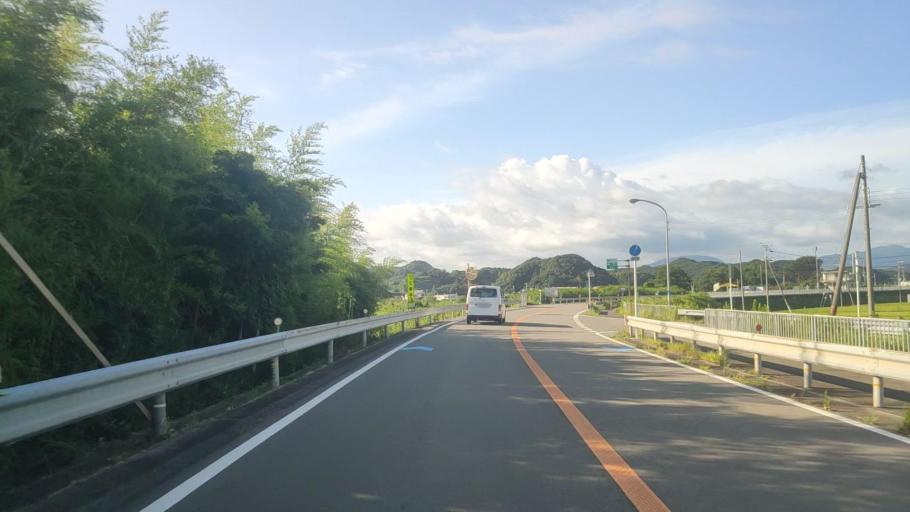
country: JP
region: Wakayama
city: Tanabe
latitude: 33.6761
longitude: 135.4076
